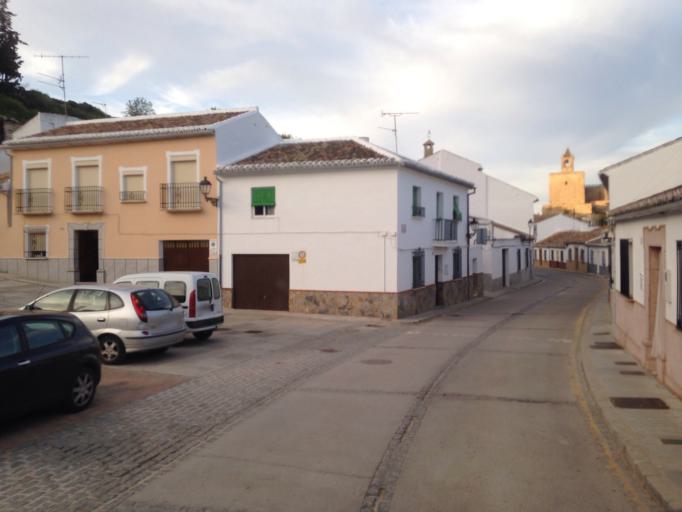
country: ES
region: Andalusia
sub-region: Provincia de Malaga
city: Antequera
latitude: 37.0114
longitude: -4.5606
